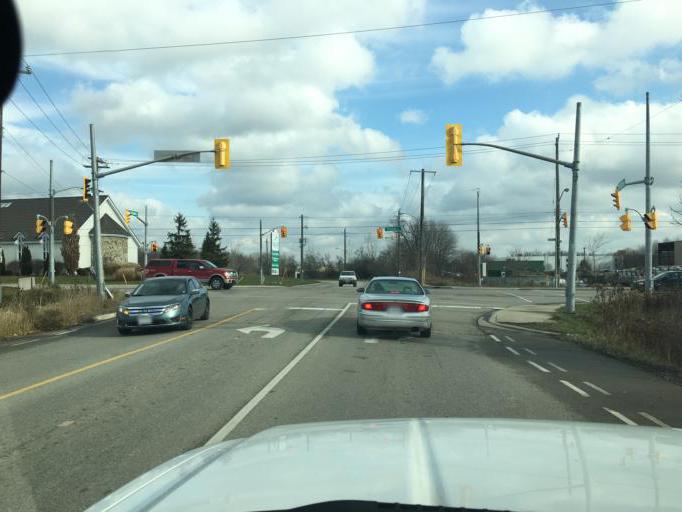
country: CA
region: Ontario
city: Waterloo
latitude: 43.5047
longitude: -80.5560
